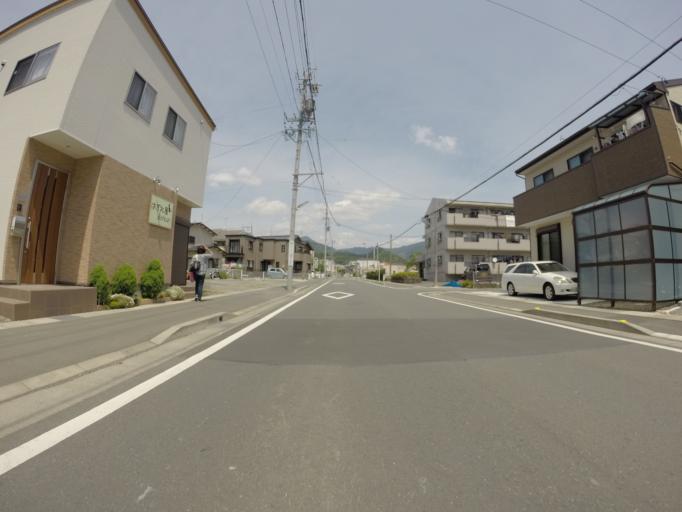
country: JP
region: Shizuoka
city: Shizuoka-shi
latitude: 35.0213
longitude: 138.4229
